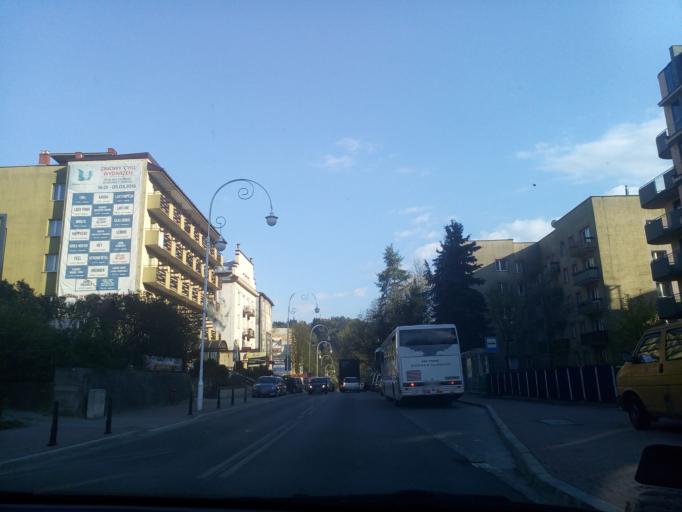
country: PL
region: Lesser Poland Voivodeship
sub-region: Powiat nowosadecki
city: Krynica-Zdroj
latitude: 49.4257
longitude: 20.9552
